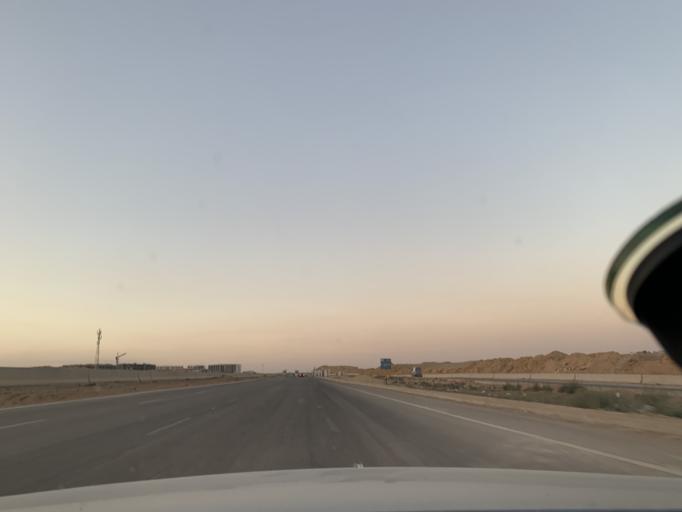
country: EG
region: Muhafazat al Qahirah
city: Halwan
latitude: 29.9604
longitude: 31.5455
